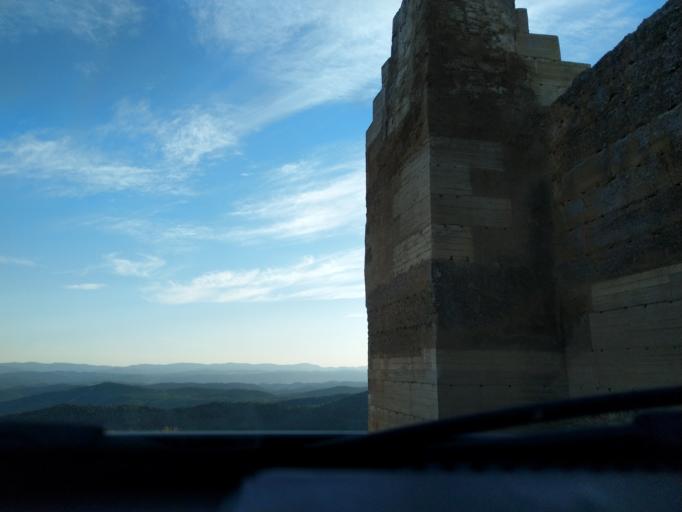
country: ES
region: Extremadura
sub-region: Provincia de Badajoz
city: Reina
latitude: 38.1891
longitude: -5.9559
